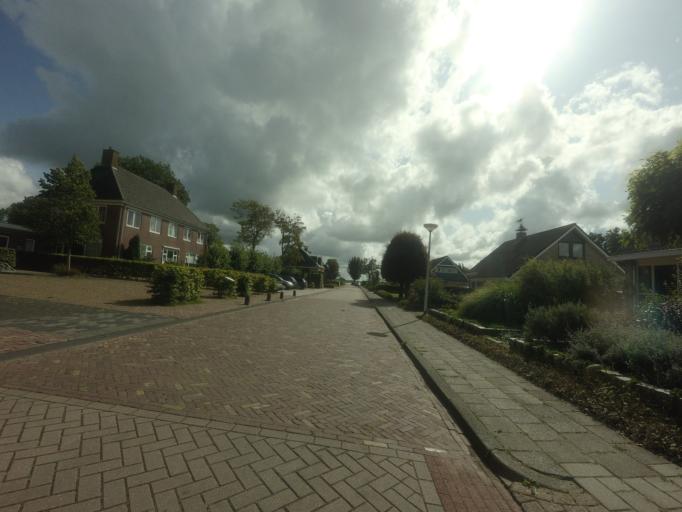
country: NL
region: Friesland
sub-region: Sudwest Fryslan
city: Scharnegoutum
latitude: 53.0763
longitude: 5.6362
